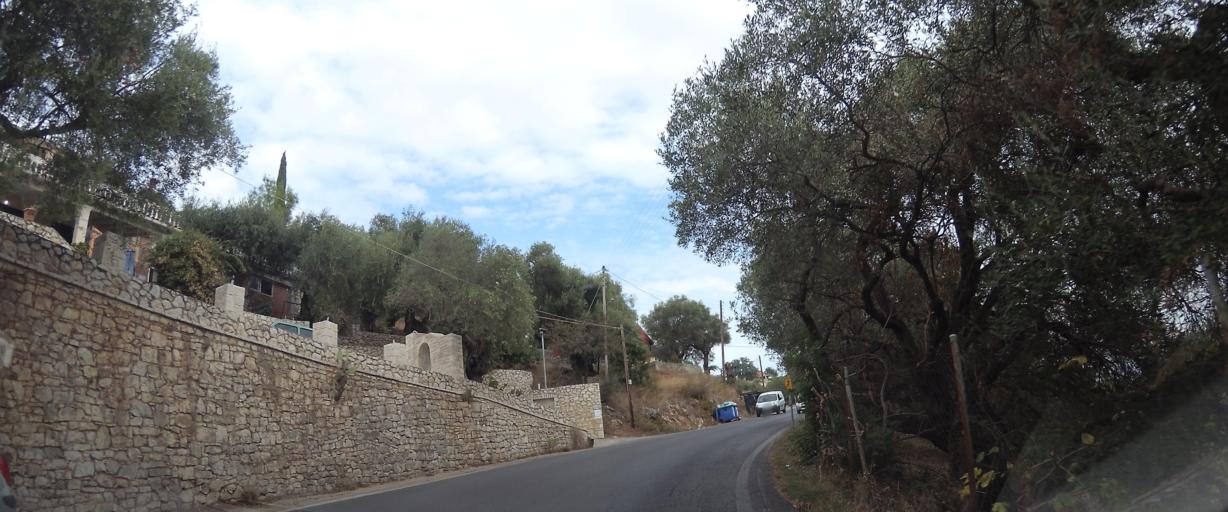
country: GR
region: Ionian Islands
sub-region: Nomos Kerkyras
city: Kontokali
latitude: 39.7256
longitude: 19.8960
